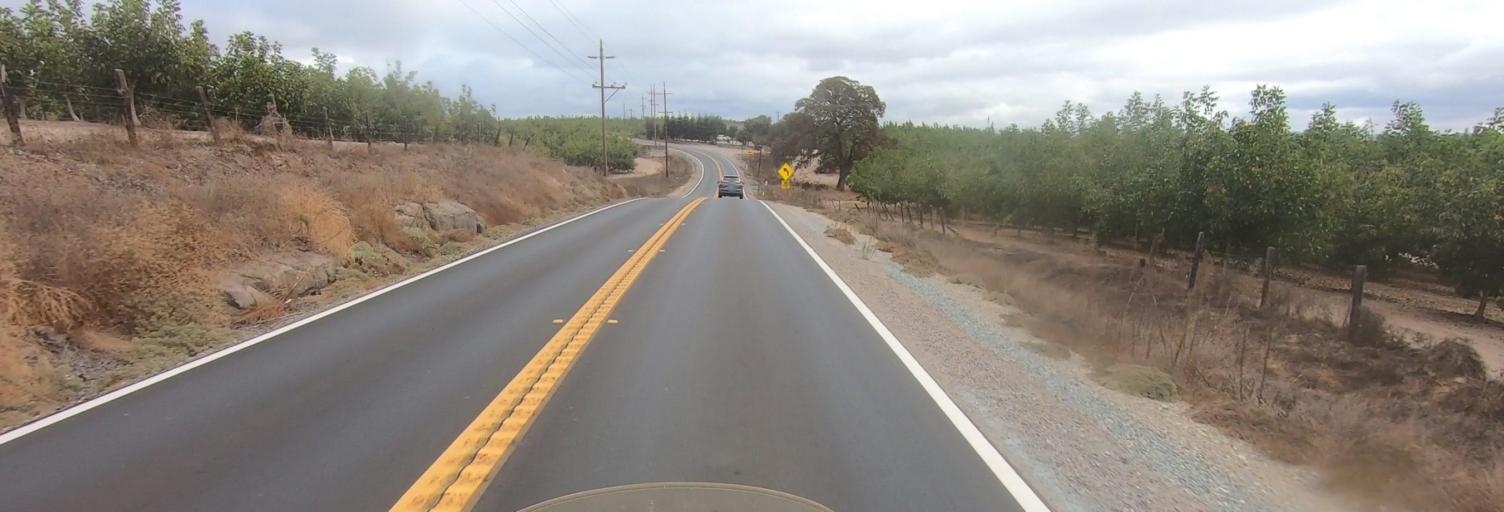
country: US
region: California
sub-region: San Joaquin County
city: Linden
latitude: 38.0717
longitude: -120.9840
